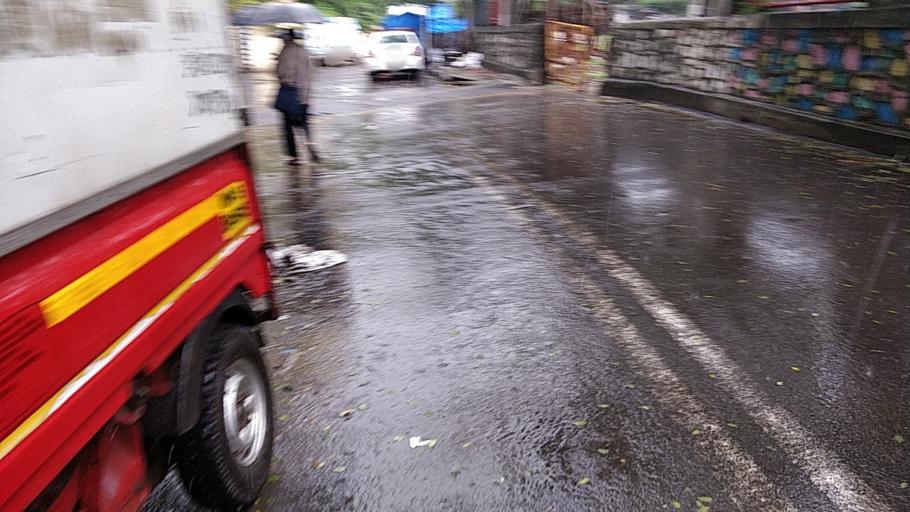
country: IN
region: Maharashtra
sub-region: Mumbai Suburban
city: Mumbai
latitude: 19.0938
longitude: 72.8404
